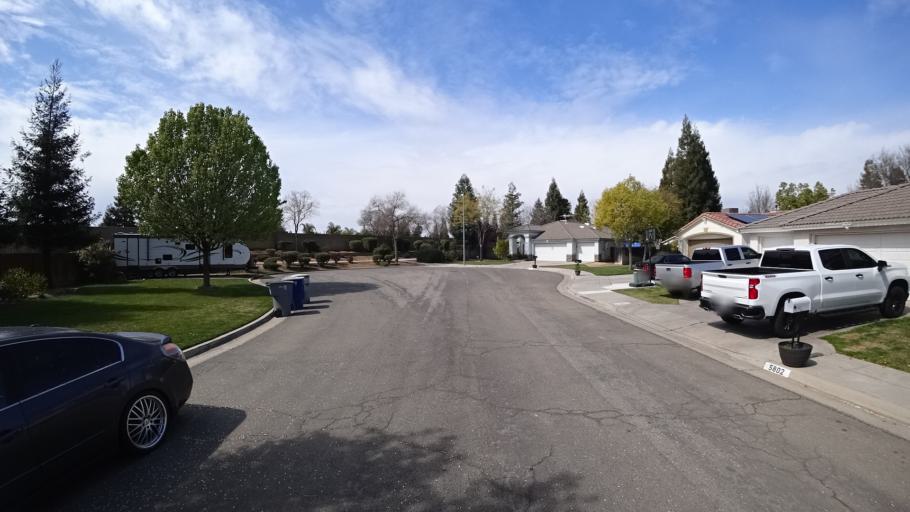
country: US
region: California
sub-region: Fresno County
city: Biola
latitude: 36.8438
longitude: -119.8951
